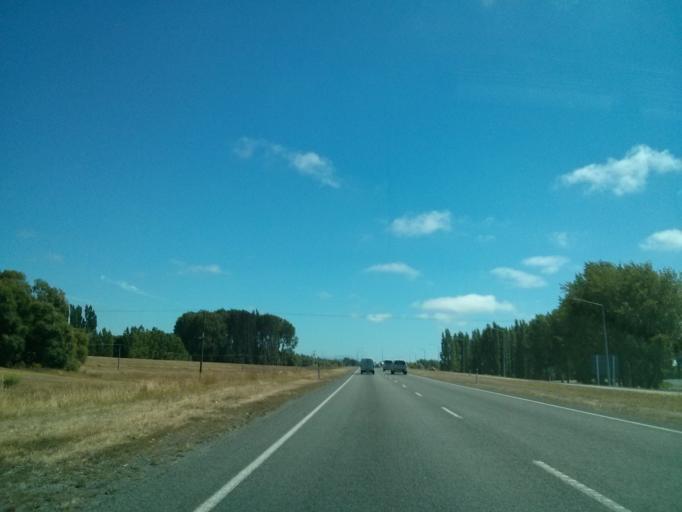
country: NZ
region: Canterbury
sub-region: Waimakariri District
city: Kaiapoi
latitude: -43.4208
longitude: 172.6482
